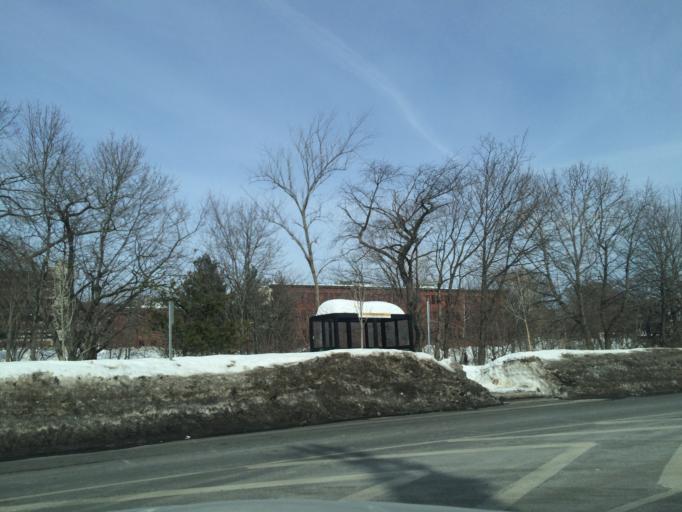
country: US
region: Massachusetts
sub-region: Middlesex County
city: Watertown
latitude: 42.3645
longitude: -71.1872
